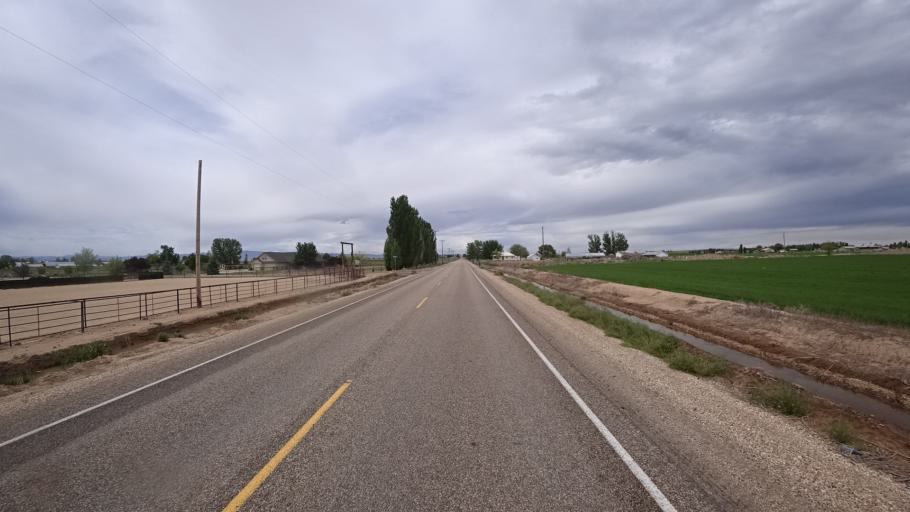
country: US
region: Idaho
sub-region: Canyon County
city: Nampa
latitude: 43.4593
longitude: -116.5187
